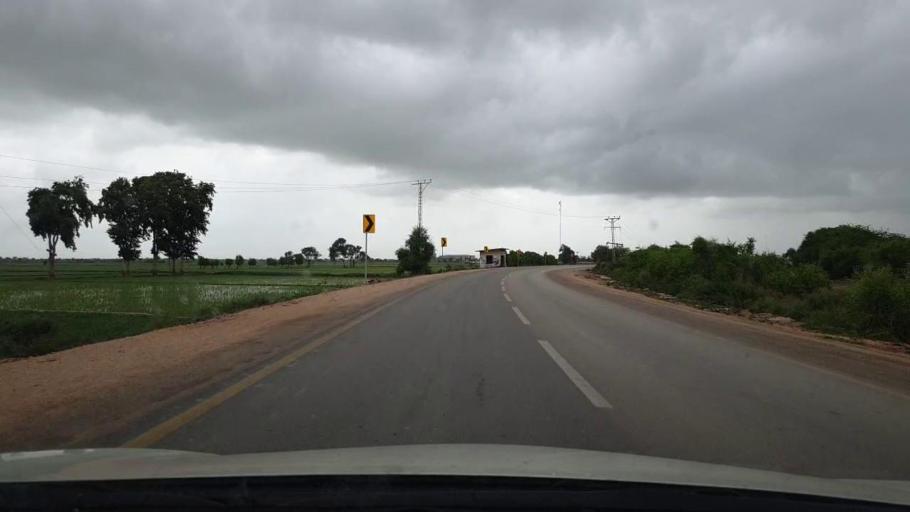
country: PK
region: Sindh
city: Kario
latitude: 24.6519
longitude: 68.4990
